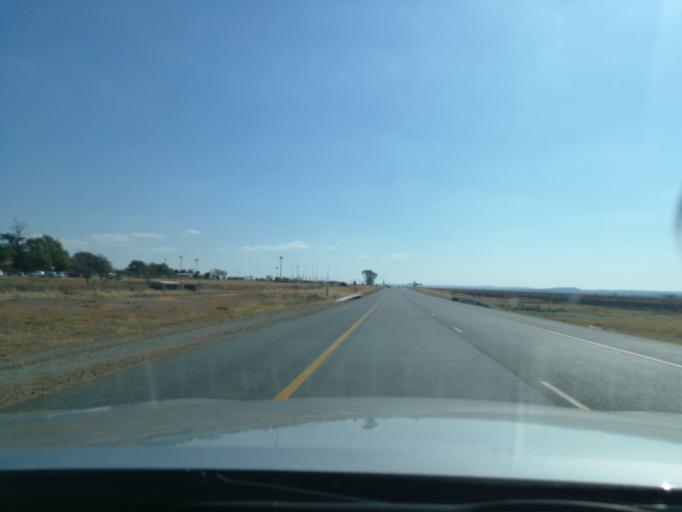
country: ZA
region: North-West
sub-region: Dr Kenneth Kaunda District Municipality
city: Klerksdorp
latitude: -26.8635
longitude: 26.5924
